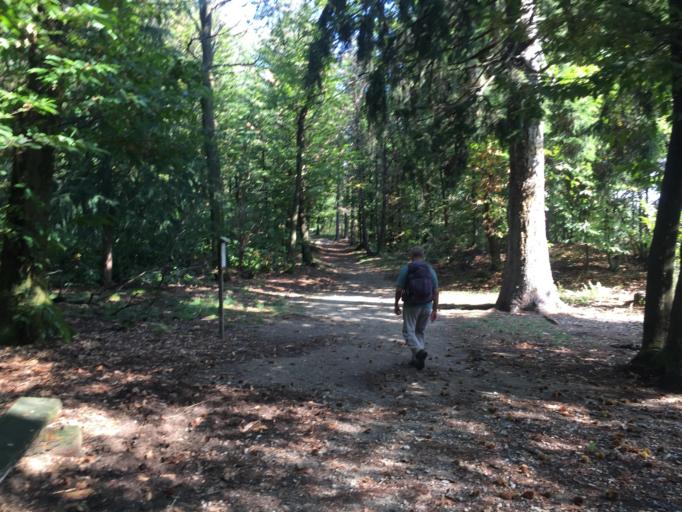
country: IT
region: Piedmont
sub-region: Provincia Verbano-Cusio-Ossola
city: Ghiffa
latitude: 45.9583
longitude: 8.6075
